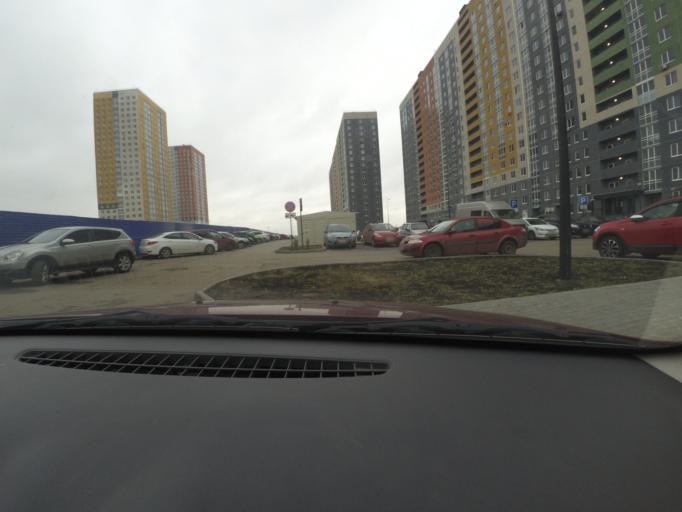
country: RU
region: Nizjnij Novgorod
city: Afonino
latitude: 56.2478
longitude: 44.0421
